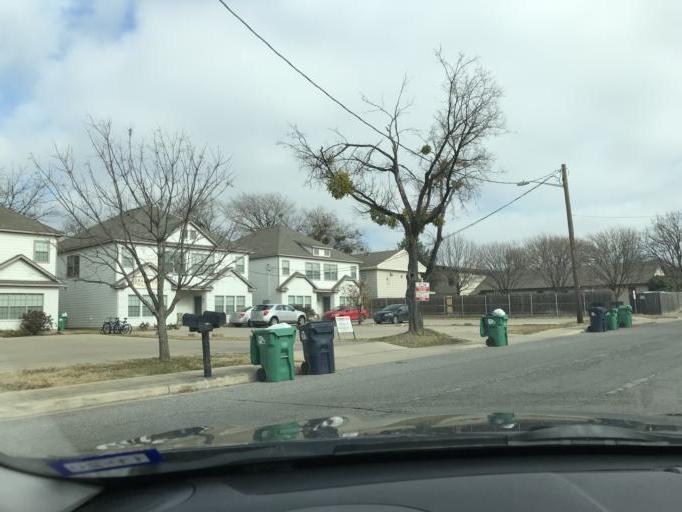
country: US
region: Texas
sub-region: Denton County
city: Denton
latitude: 33.2108
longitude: -97.1593
